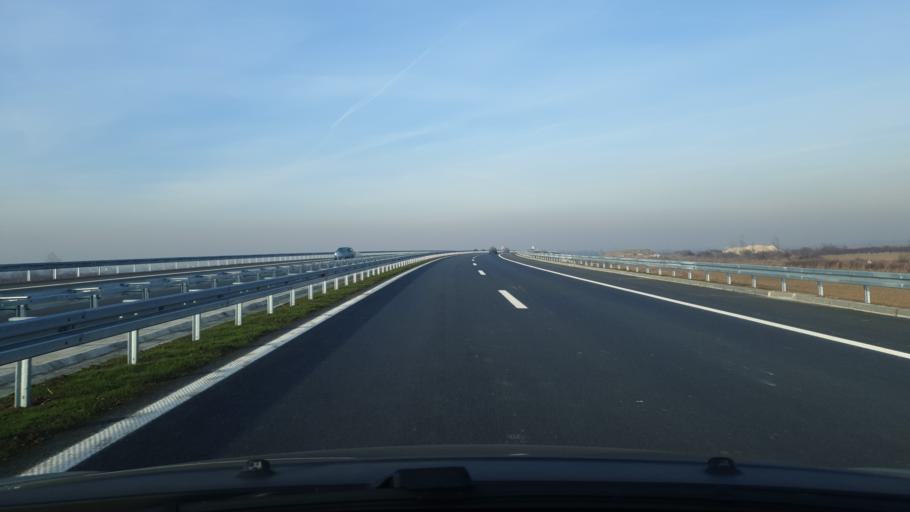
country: RS
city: Boljevci
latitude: 44.7132
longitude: 20.2589
